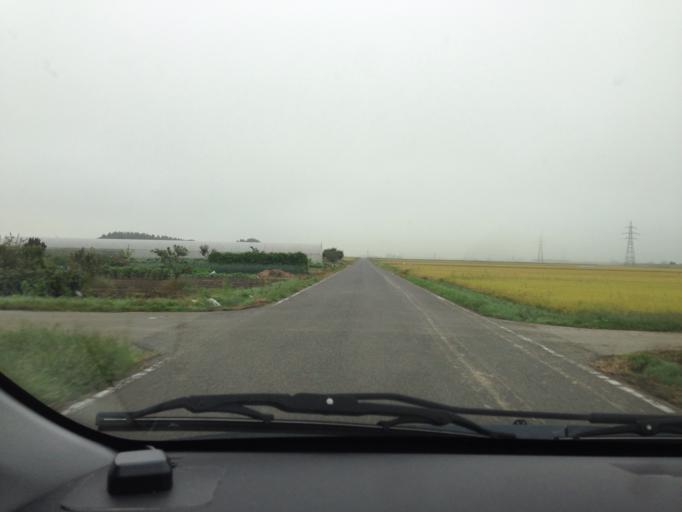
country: JP
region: Fukushima
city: Kitakata
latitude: 37.5707
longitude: 139.8663
